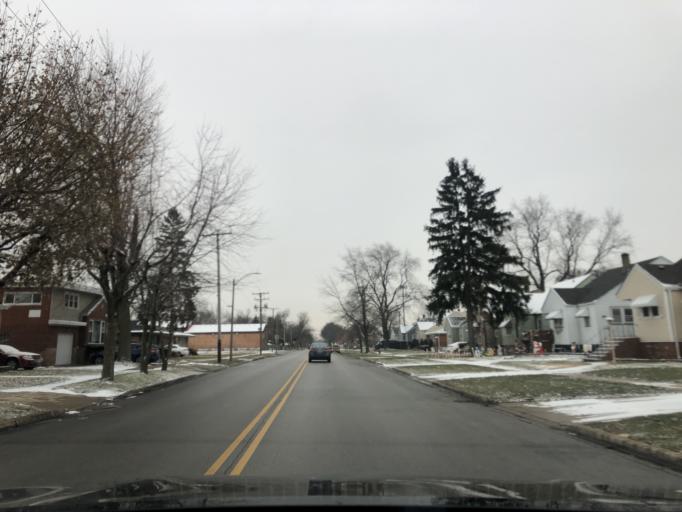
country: US
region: Illinois
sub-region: Cook County
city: Evergreen Park
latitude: 41.7333
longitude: -87.6923
